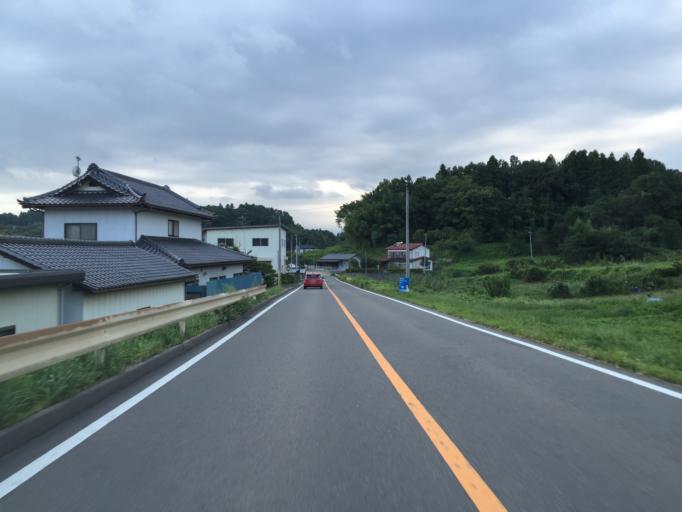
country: JP
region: Fukushima
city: Fukushima-shi
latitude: 37.6657
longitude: 140.5187
